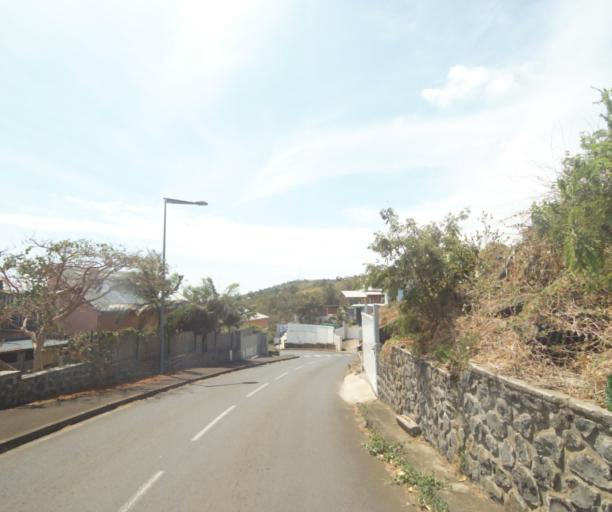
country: RE
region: Reunion
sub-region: Reunion
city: Trois-Bassins
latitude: -21.0988
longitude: 55.2725
